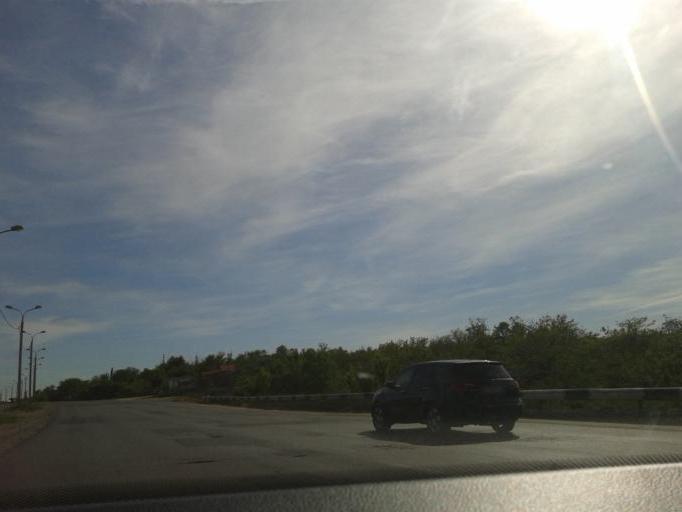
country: RU
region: Volgograd
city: Volgograd
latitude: 48.7303
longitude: 44.4513
